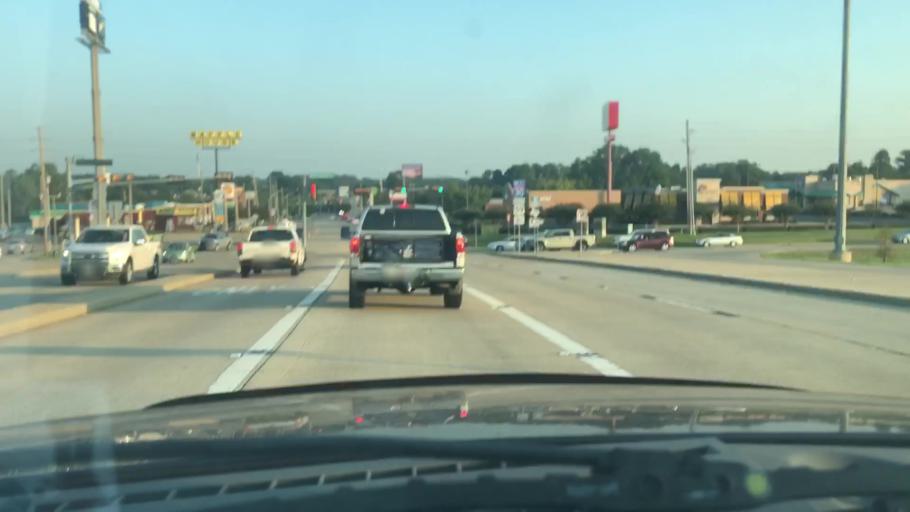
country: US
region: Arkansas
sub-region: Miller County
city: Texarkana
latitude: 33.4663
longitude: -94.0668
